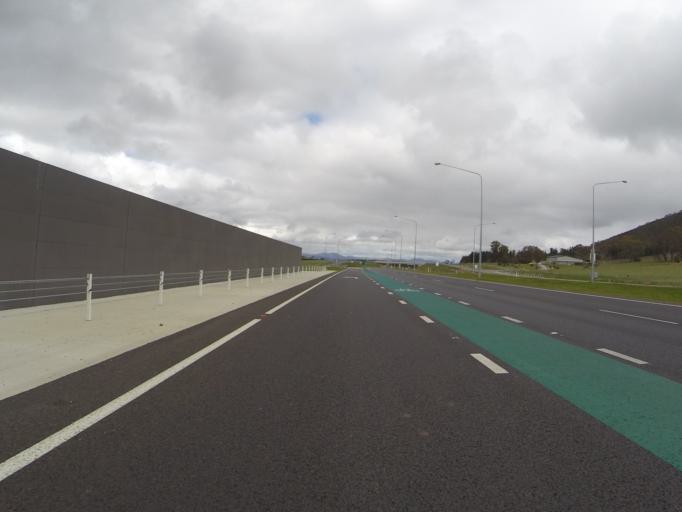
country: AU
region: Australian Capital Territory
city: Canberra
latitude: -35.2286
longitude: 149.1966
